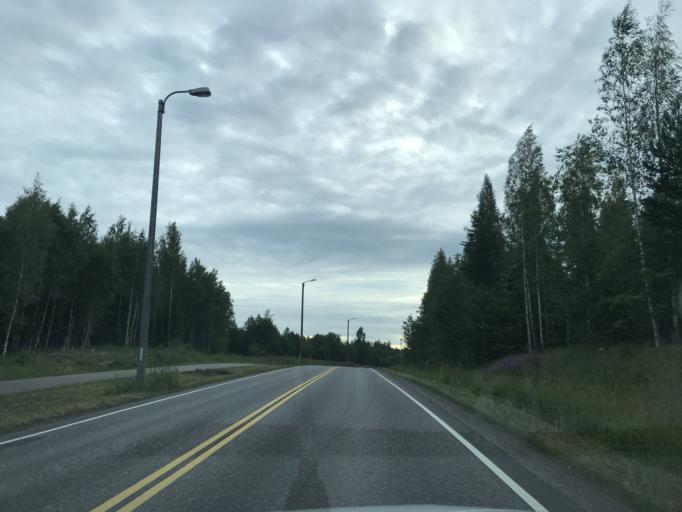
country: FI
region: Uusimaa
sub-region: Helsinki
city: Nurmijaervi
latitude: 60.3839
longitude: 24.7022
